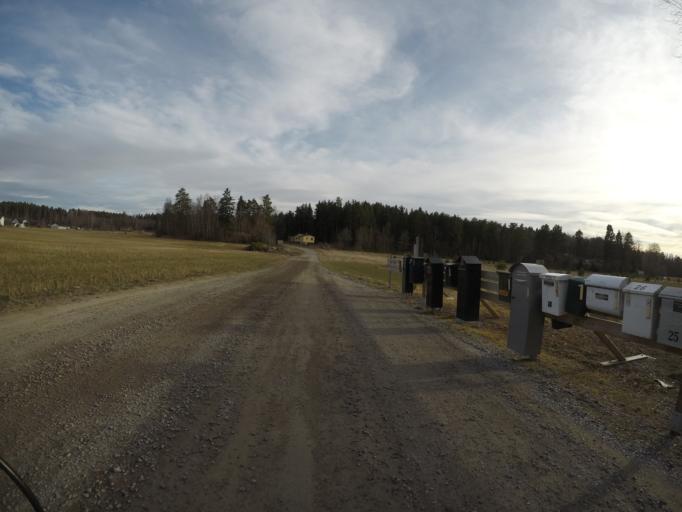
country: SE
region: Soedermanland
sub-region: Eskilstuna Kommun
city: Hallbybrunn
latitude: 59.4315
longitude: 16.4141
